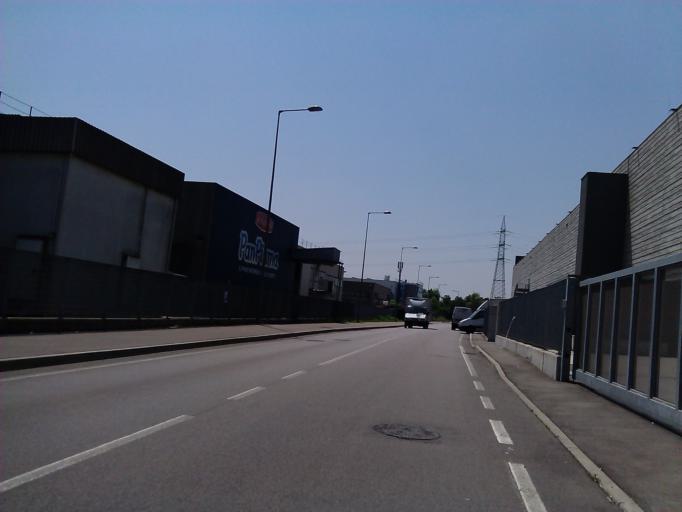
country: IT
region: Veneto
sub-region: Provincia di Venezia
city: Mestre
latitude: 45.4596
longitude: 12.2139
